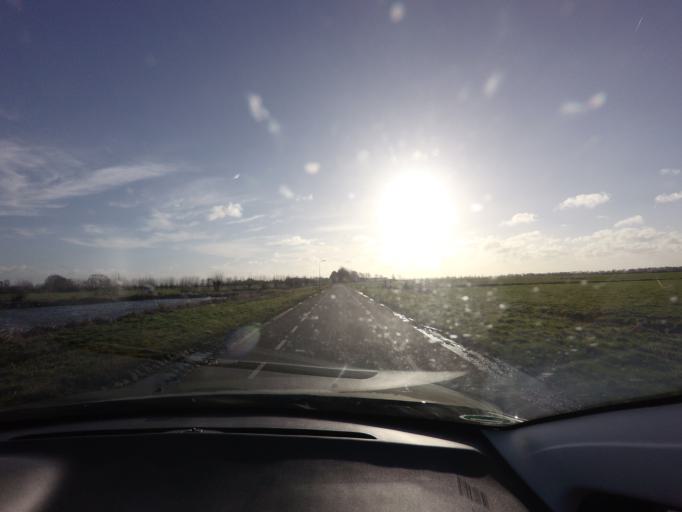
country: NL
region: Utrecht
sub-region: Stichtse Vecht
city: Breukelen
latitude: 52.1909
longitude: 4.9701
